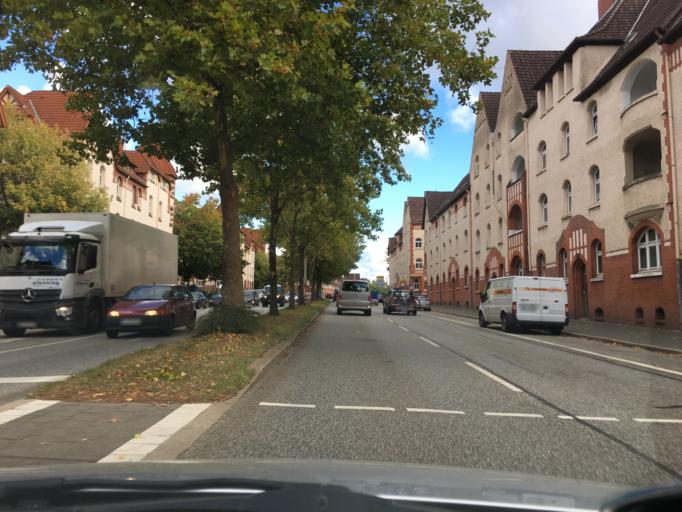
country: DE
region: Schleswig-Holstein
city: Kiel
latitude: 54.3053
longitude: 10.1481
